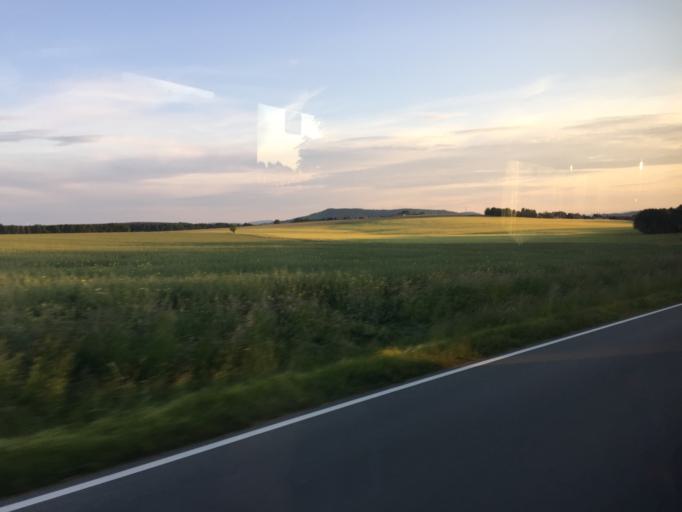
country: DE
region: Saxony
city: Reichenbach
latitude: 51.1446
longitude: 14.8267
